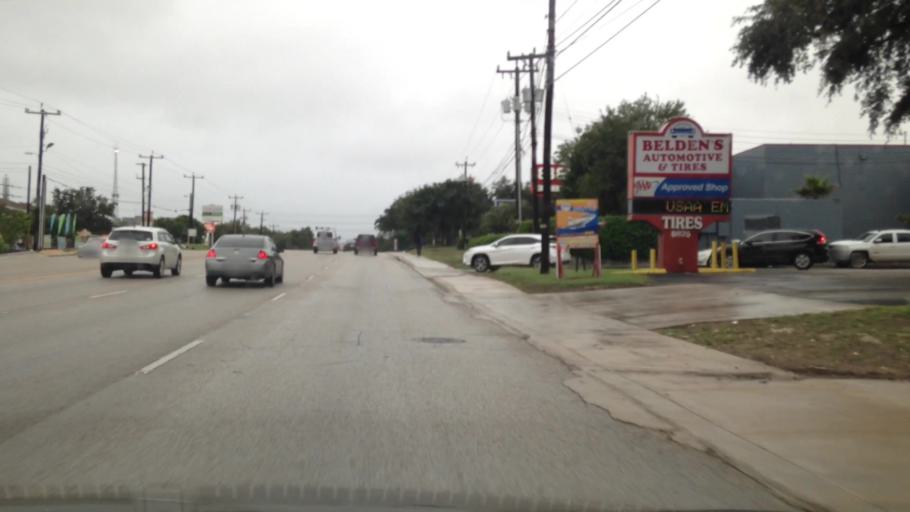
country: US
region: Texas
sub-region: Bexar County
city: Balcones Heights
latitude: 29.5257
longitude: -98.5751
